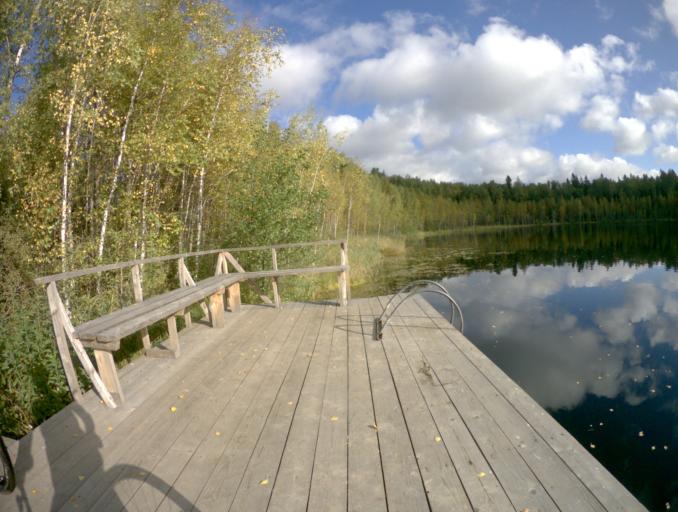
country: RU
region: Vladimir
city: Lakinsk
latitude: 55.9461
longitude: 39.7982
